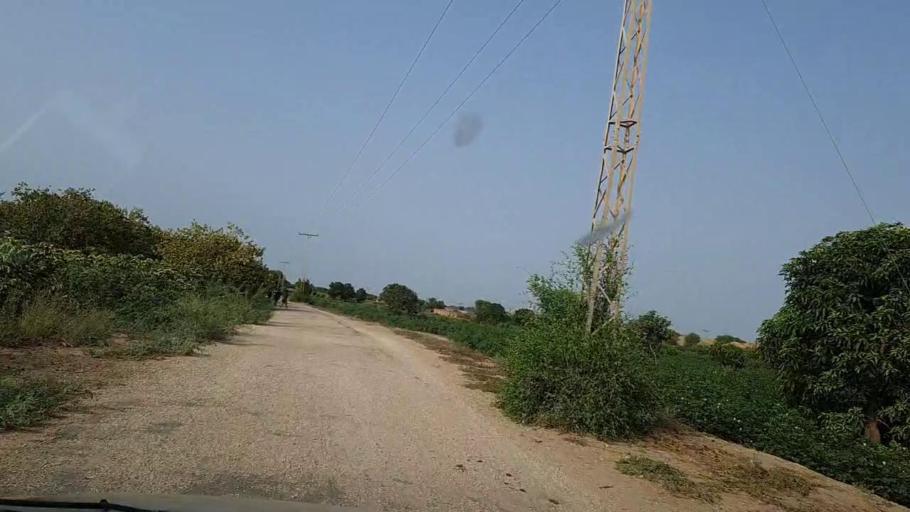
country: PK
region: Sindh
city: Kotri
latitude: 25.2305
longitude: 68.2576
